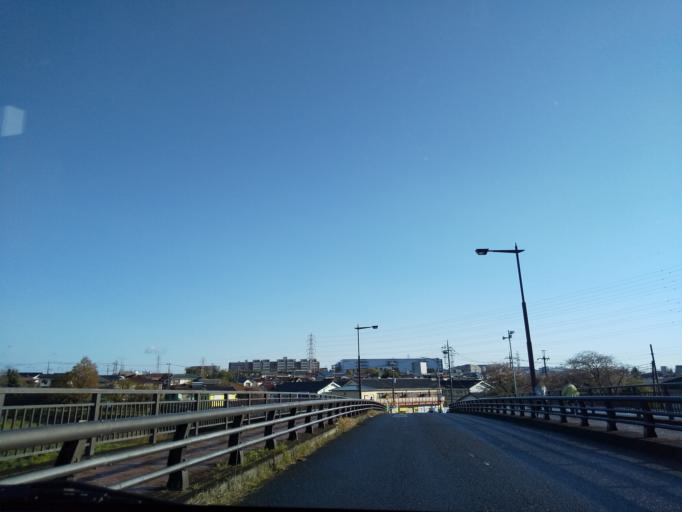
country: JP
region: Tokyo
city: Hino
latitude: 35.6451
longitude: 139.3666
